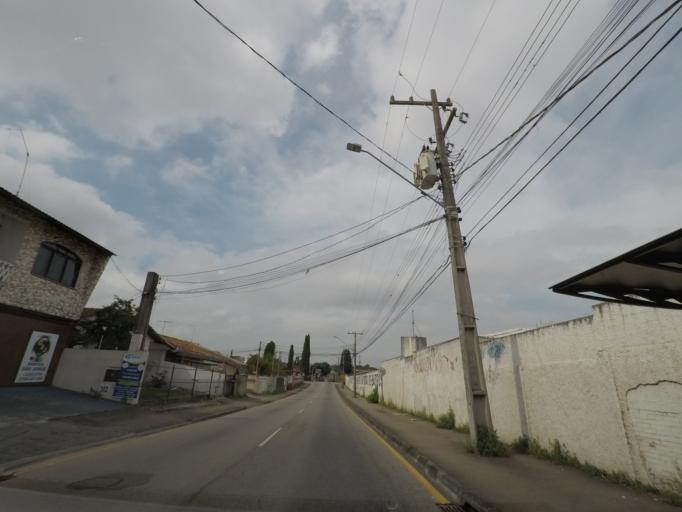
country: BR
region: Parana
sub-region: Curitiba
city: Curitiba
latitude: -25.4959
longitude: -49.2808
